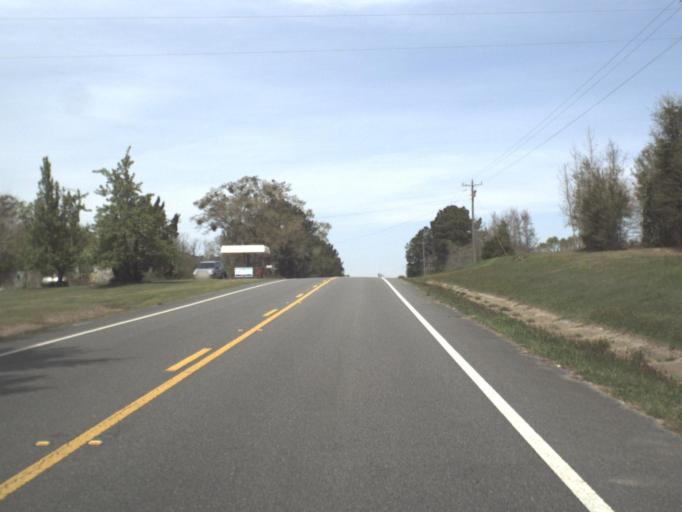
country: US
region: Alabama
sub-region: Geneva County
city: Geneva
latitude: 30.9079
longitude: -85.9573
